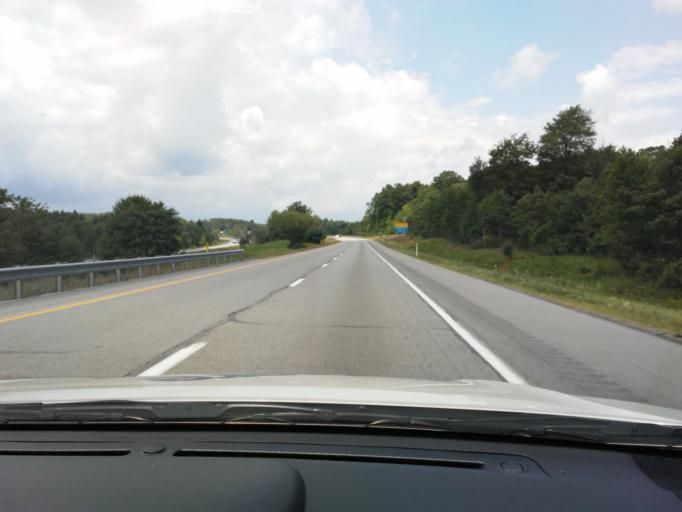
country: US
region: Pennsylvania
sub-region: Clearfield County
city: Troy
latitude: 40.9763
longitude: -78.1234
